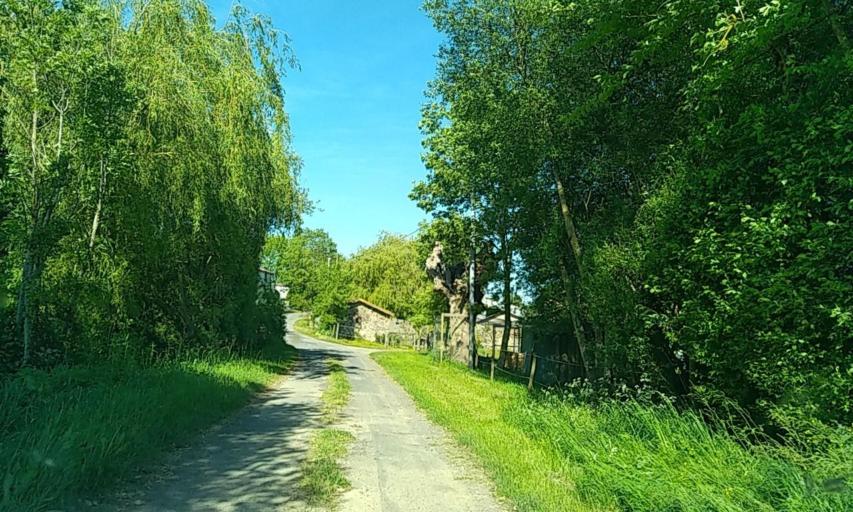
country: FR
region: Poitou-Charentes
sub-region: Departement des Deux-Sevres
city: Boisme
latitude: 46.7922
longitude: -0.4457
